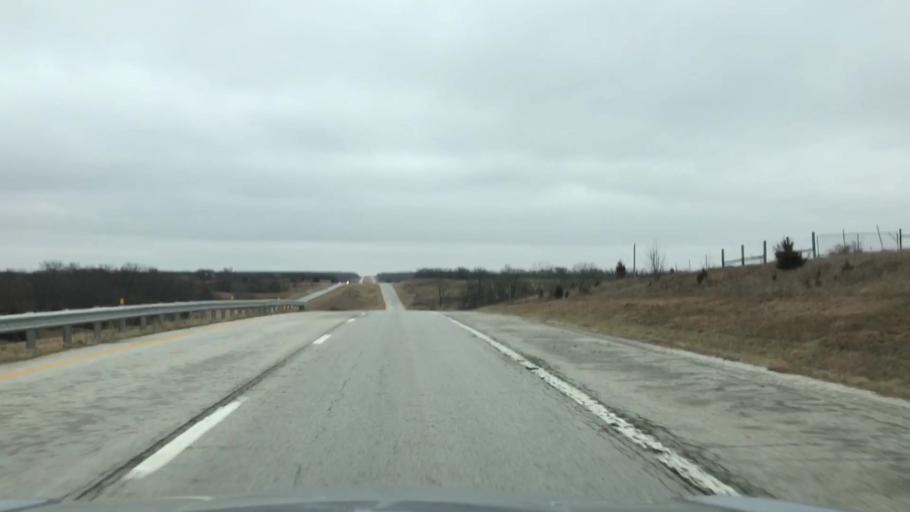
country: US
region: Missouri
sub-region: Linn County
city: Marceline
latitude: 39.7591
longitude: -92.8804
